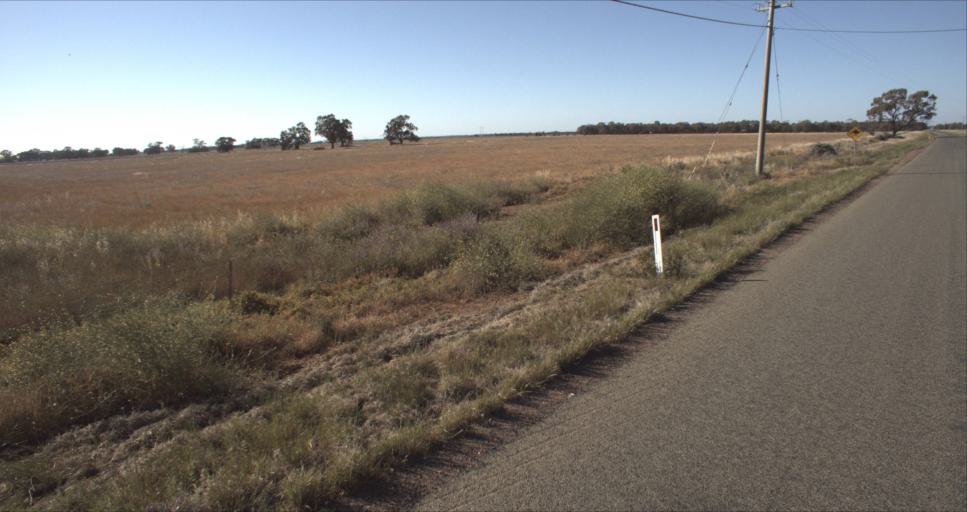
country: AU
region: New South Wales
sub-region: Leeton
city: Leeton
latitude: -34.5548
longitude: 146.2666
